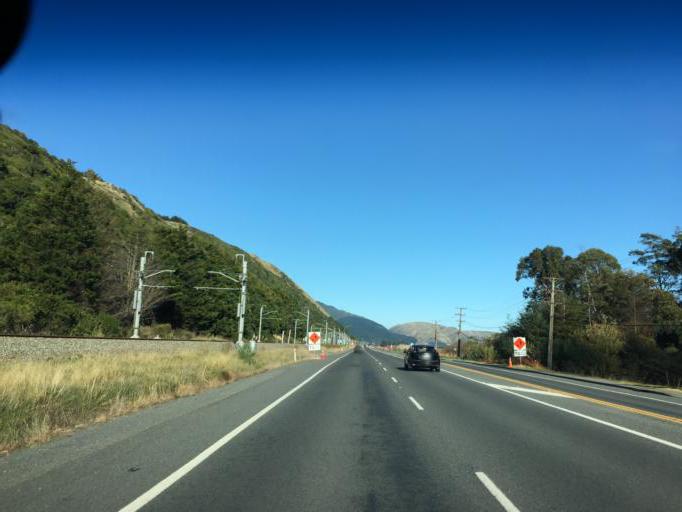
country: NZ
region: Wellington
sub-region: Kapiti Coast District
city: Paraparaumu
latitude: -40.9330
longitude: 174.9963
